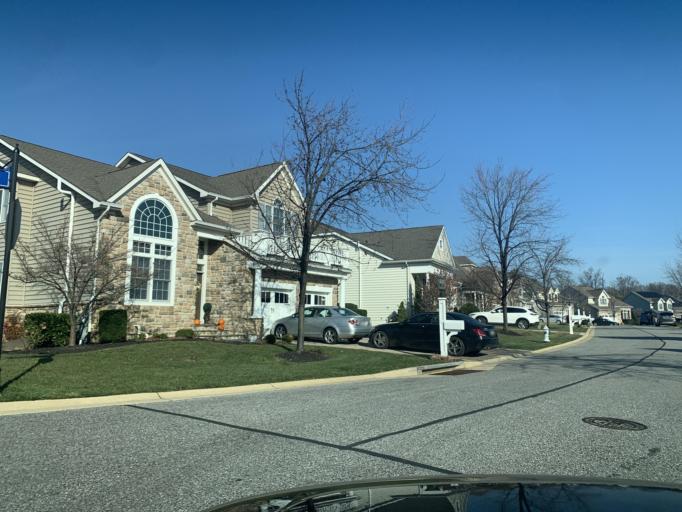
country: US
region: Maryland
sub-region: Harford County
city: Havre de Grace
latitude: 39.5526
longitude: -76.1259
